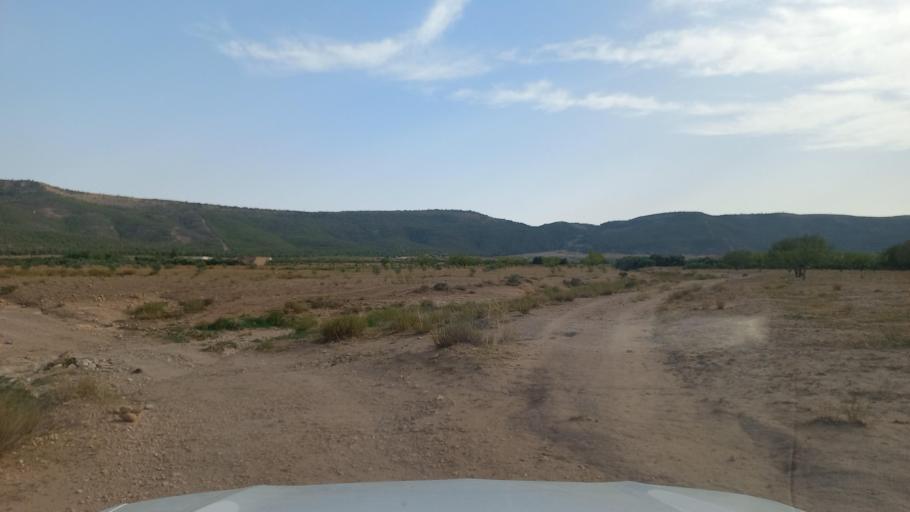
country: TN
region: Al Qasrayn
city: Kasserine
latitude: 35.3554
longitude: 8.8540
